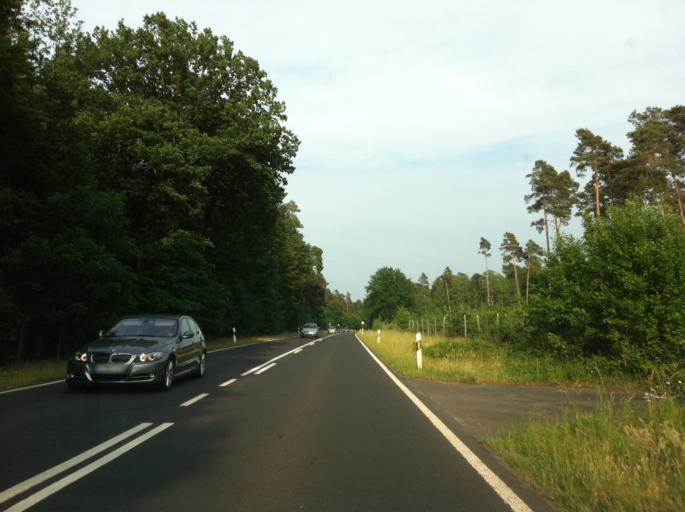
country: DE
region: Bavaria
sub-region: Regierungsbezirk Unterfranken
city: Stockstadt am Main
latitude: 49.9587
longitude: 9.0389
